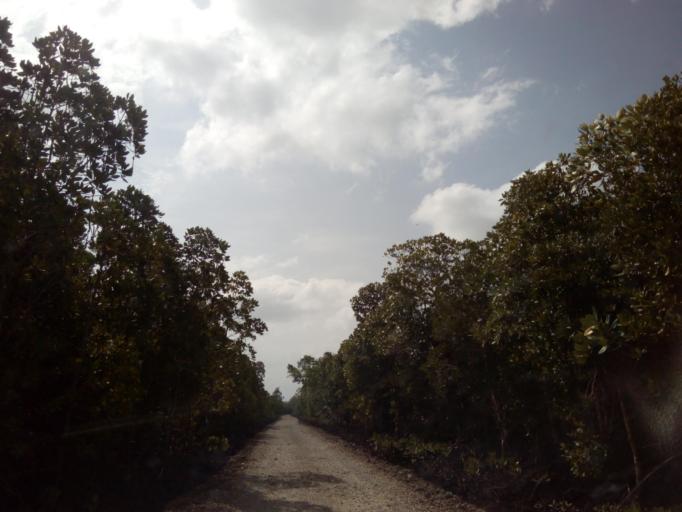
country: TZ
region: Zanzibar Central/South
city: Mahonda
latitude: -6.3145
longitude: 39.3838
